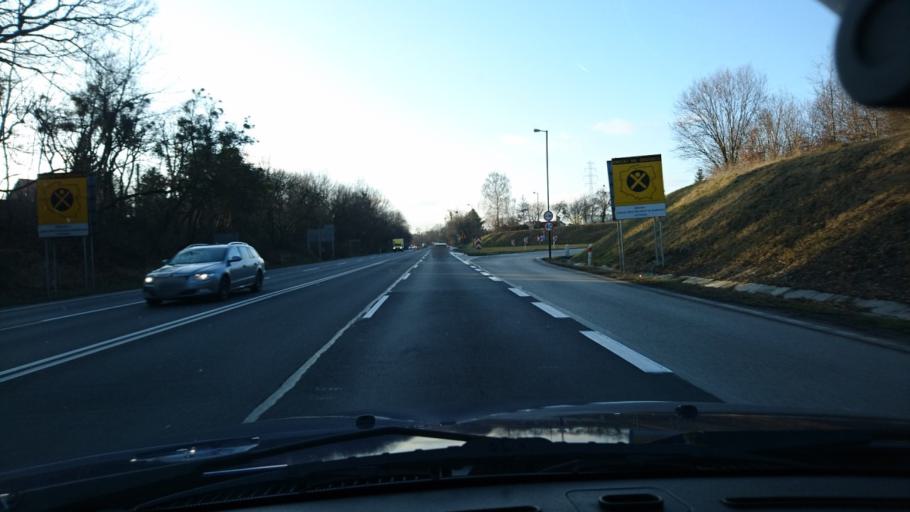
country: PL
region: Silesian Voivodeship
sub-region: Gliwice
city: Gliwice
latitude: 50.3152
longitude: 18.6929
